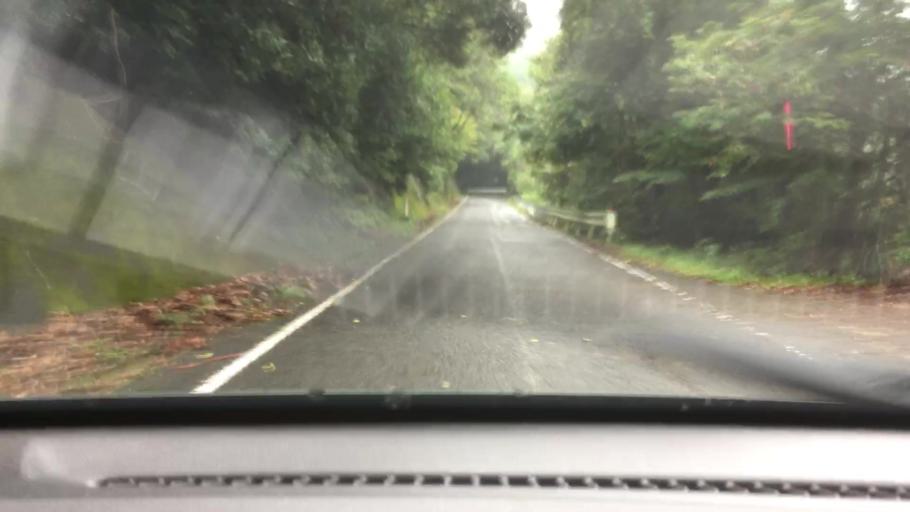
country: JP
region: Nagasaki
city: Togitsu
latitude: 32.9219
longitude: 129.7263
